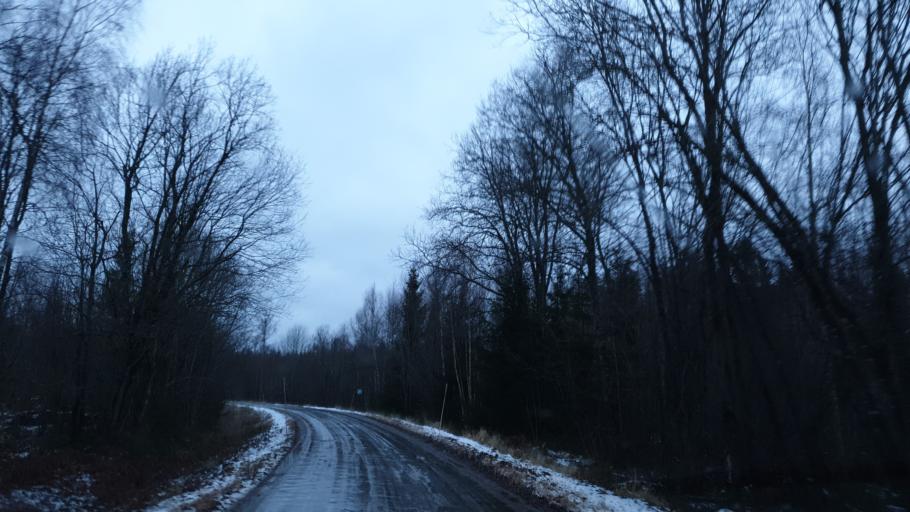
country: SE
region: Uppsala
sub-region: Tierps Kommun
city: Tierp
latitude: 60.3459
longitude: 17.4683
